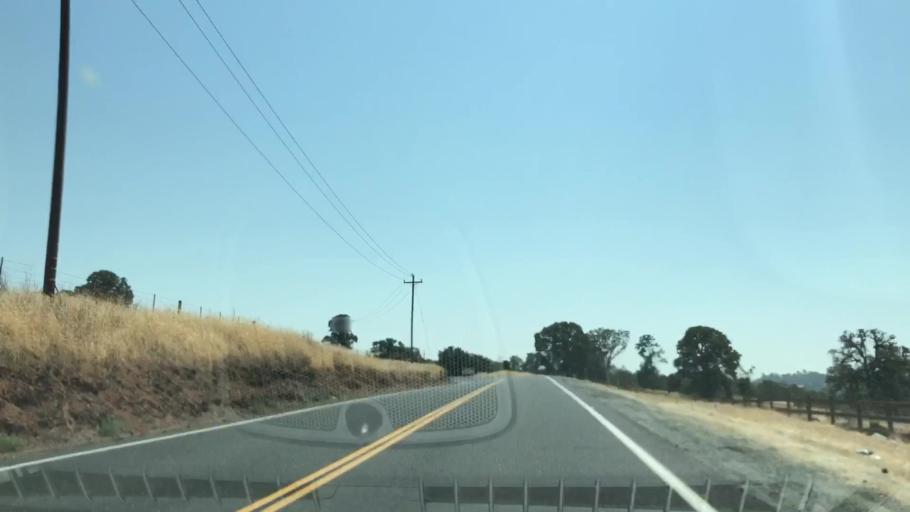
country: US
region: California
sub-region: Calaveras County
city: Copperopolis
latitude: 37.9260
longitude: -120.5966
